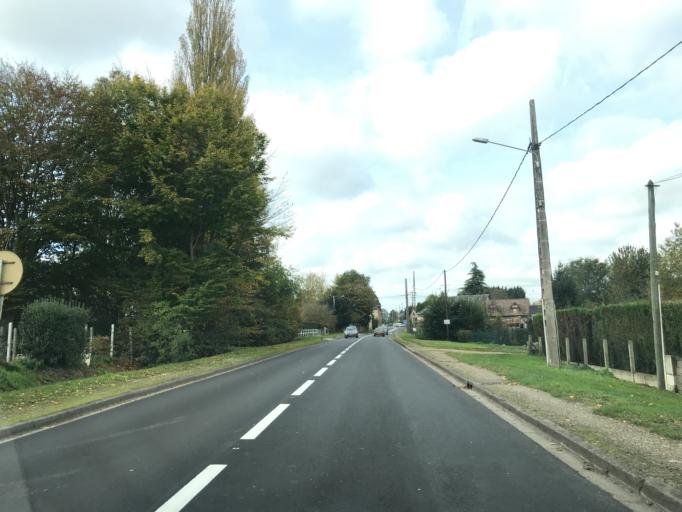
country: FR
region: Haute-Normandie
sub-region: Departement de l'Eure
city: Fleury-sur-Andelle
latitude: 49.3428
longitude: 1.3702
